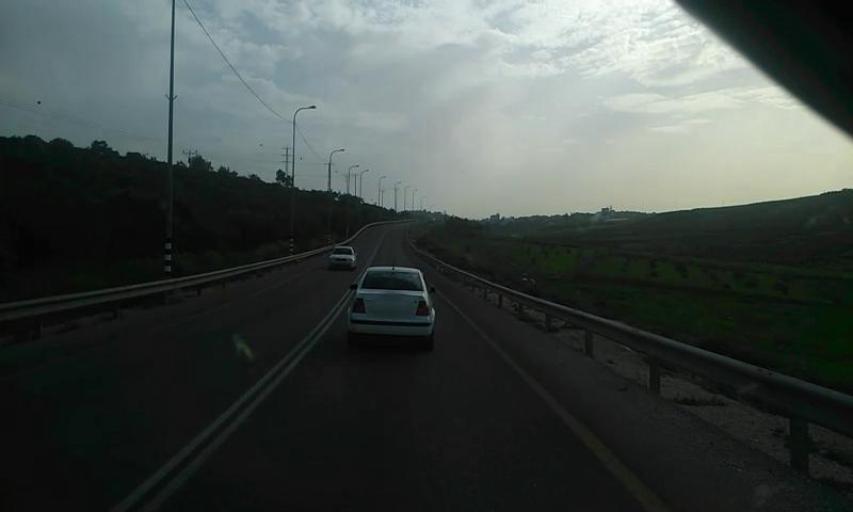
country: PS
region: West Bank
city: Immatin
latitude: 32.1999
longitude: 35.1482
